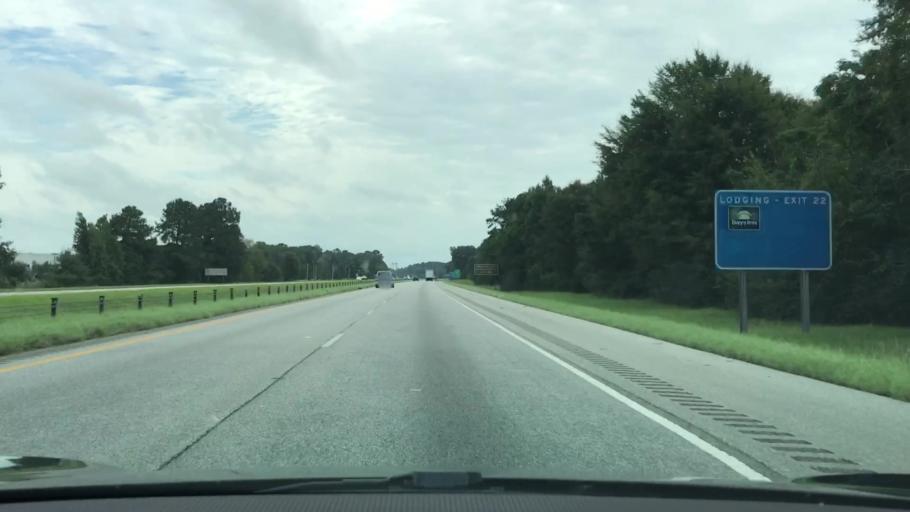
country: US
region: Alabama
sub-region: Elmore County
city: Tallassee
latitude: 32.4000
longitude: -85.9715
